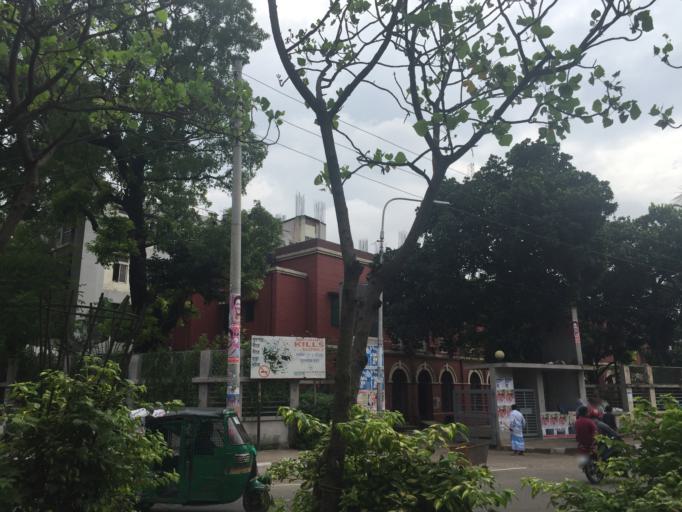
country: BD
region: Dhaka
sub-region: Dhaka
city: Dhaka
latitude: 23.7247
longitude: 90.4048
